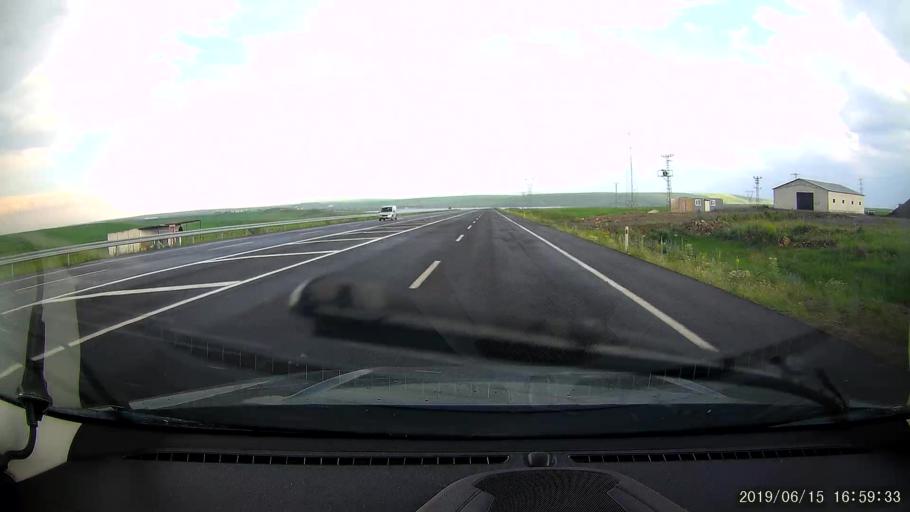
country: TR
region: Kars
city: Susuz
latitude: 40.7504
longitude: 43.1515
